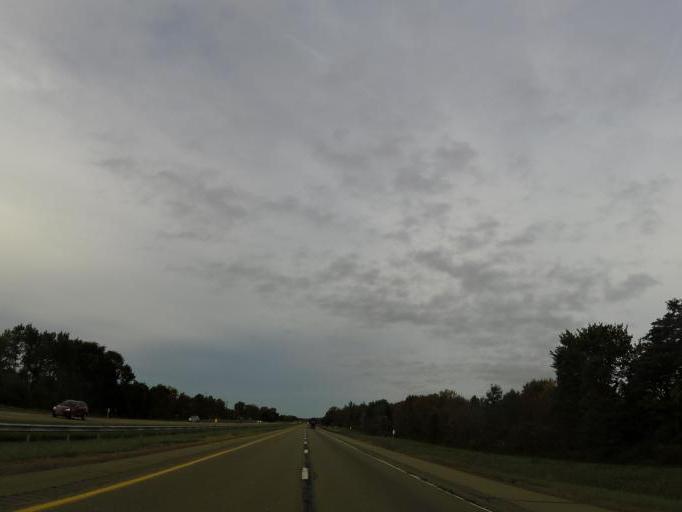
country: US
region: New York
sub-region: Chautauqua County
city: Silver Creek
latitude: 42.5083
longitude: -79.2091
